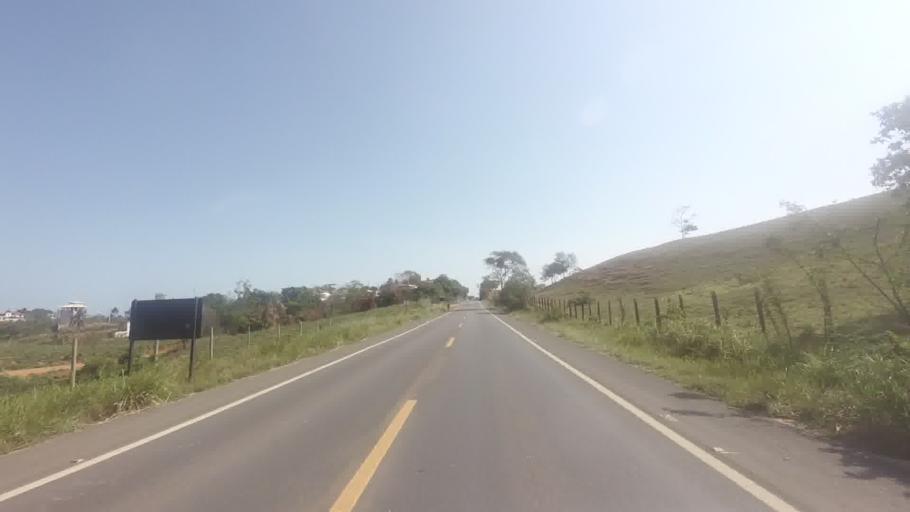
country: BR
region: Espirito Santo
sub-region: Piuma
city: Piuma
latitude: -20.8275
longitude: -40.7005
